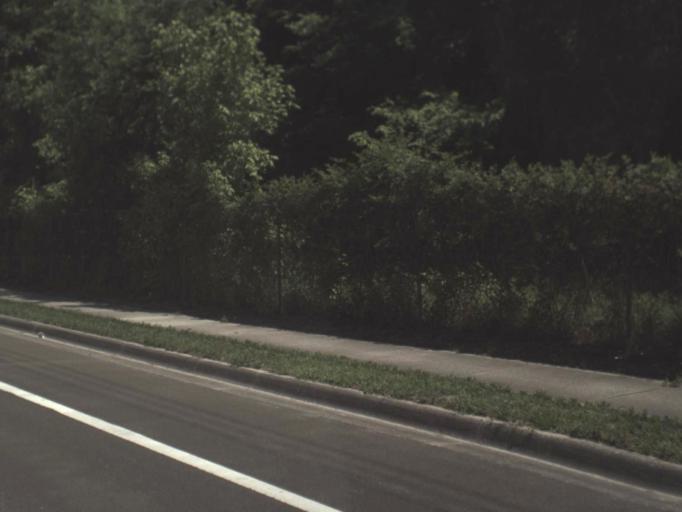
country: US
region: Florida
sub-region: Alachua County
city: Gainesville
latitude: 29.6477
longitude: -82.2990
